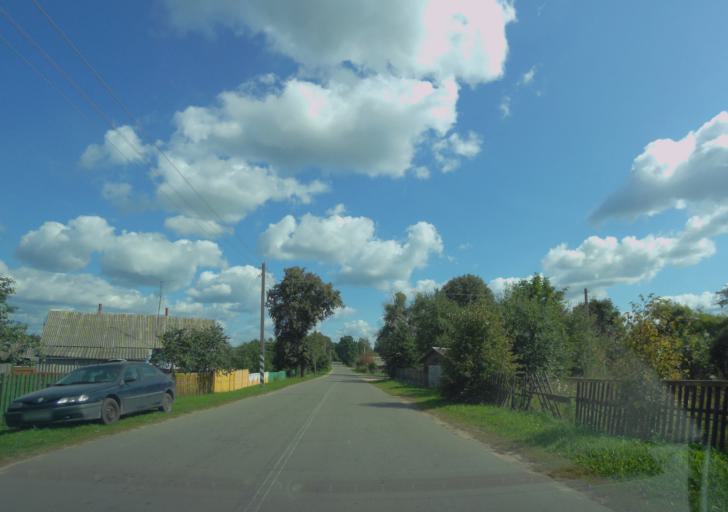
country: BY
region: Minsk
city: Zyembin
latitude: 54.4258
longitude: 28.4234
